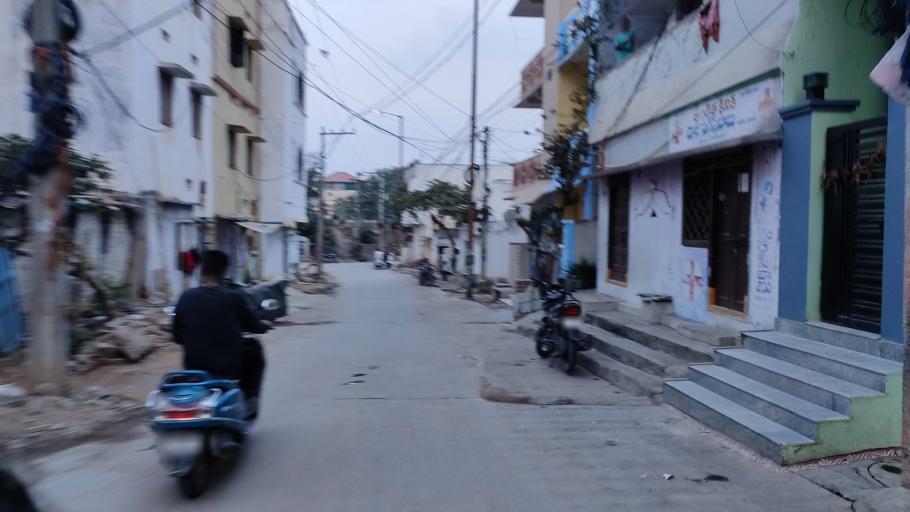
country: IN
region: Telangana
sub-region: Hyderabad
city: Malkajgiri
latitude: 17.4459
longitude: 78.5228
